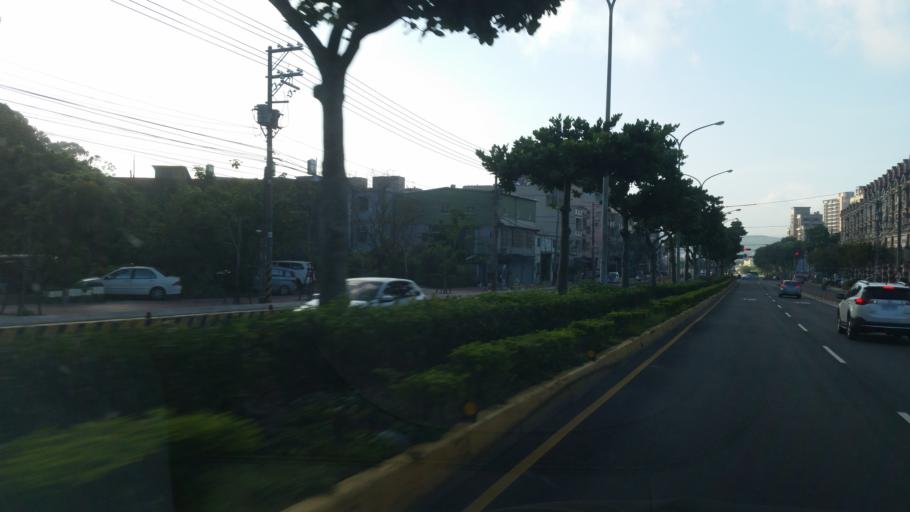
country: TW
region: Taiwan
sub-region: Taoyuan
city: Taoyuan
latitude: 25.0085
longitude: 121.3449
